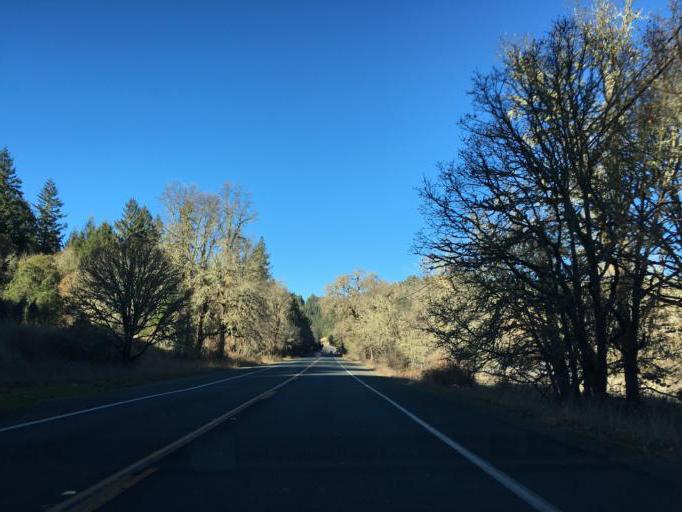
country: US
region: California
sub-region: Mendocino County
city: Brooktrails
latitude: 39.4569
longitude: -123.3486
